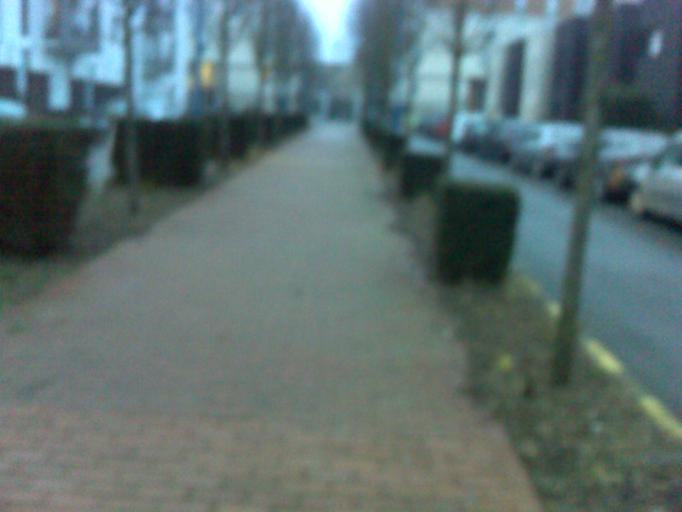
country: FR
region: Nord-Pas-de-Calais
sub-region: Departement du Nord
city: Halluin
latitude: 50.7864
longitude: 3.1249
